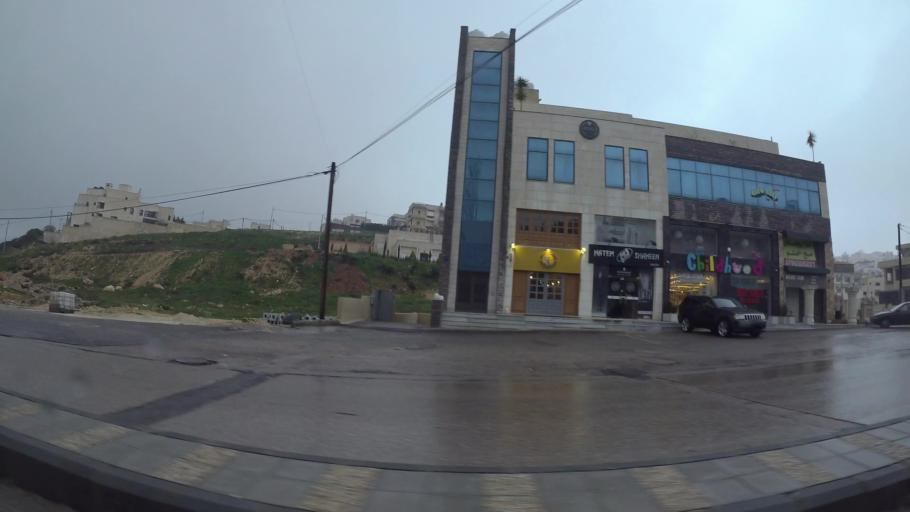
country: JO
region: Amman
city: Al Jubayhah
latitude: 32.0088
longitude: 35.8329
